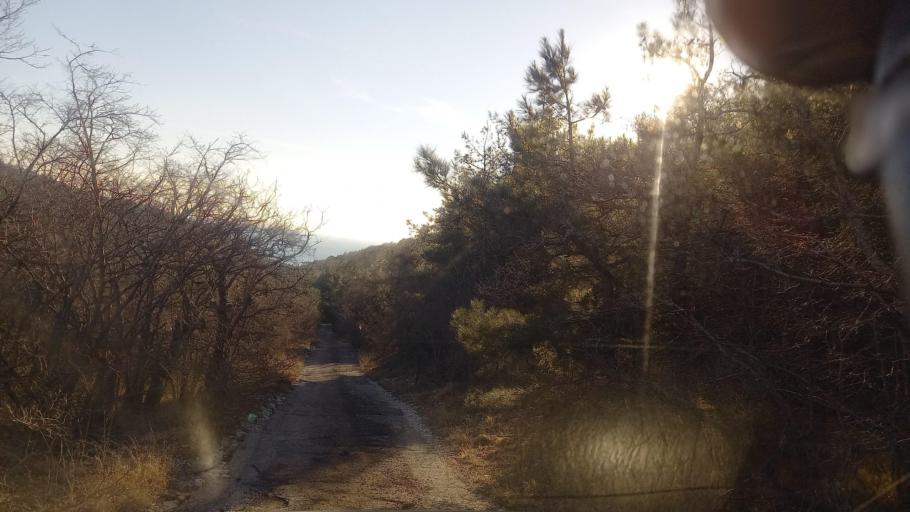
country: RU
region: Krasnodarskiy
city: Kabardinka
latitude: 44.6126
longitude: 37.9416
